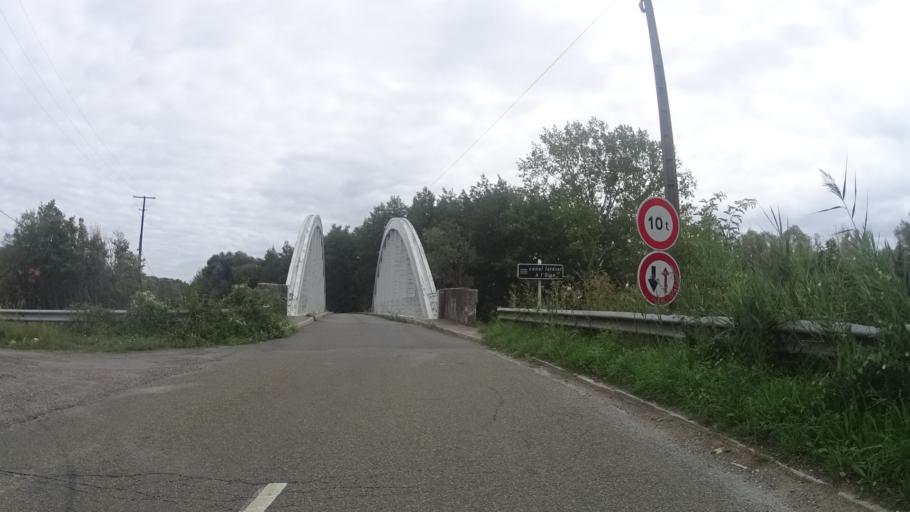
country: FR
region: Picardie
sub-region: Departement de l'Oise
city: Chiry-Ourscamp
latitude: 49.5344
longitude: 2.9604
